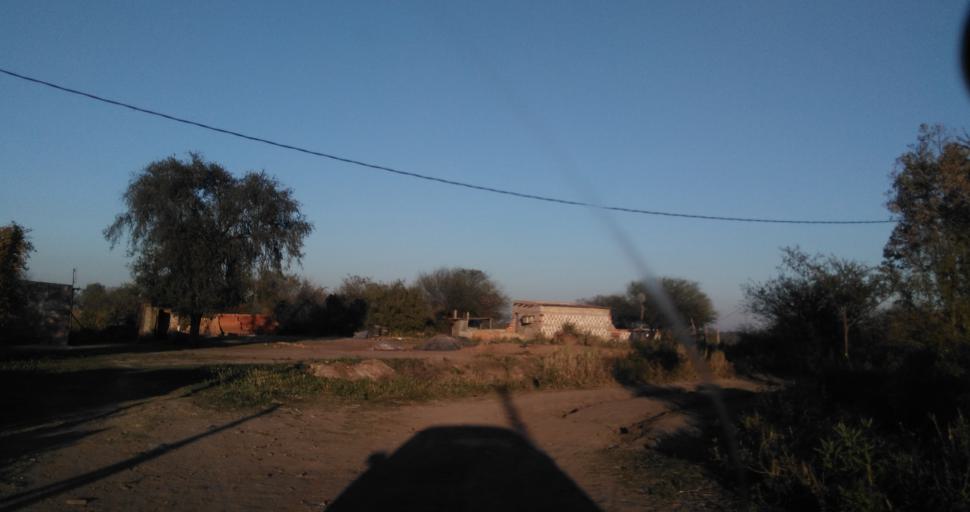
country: AR
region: Chaco
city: Fontana
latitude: -27.4339
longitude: -59.0319
